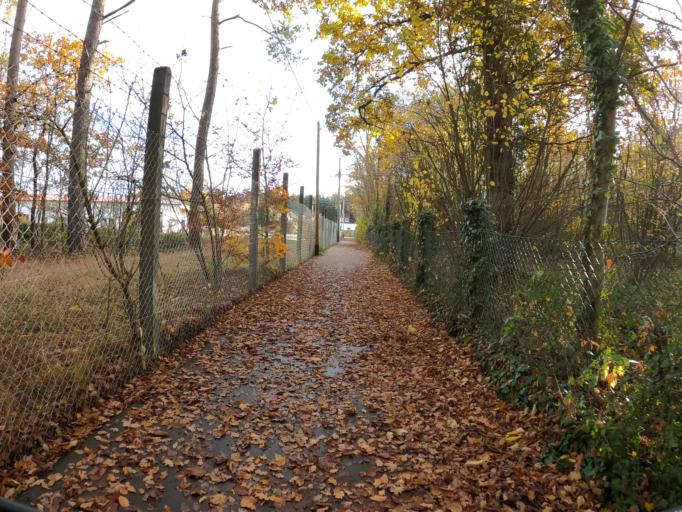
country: DE
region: Bavaria
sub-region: Swabia
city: Nersingen
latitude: 48.4138
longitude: 10.1532
